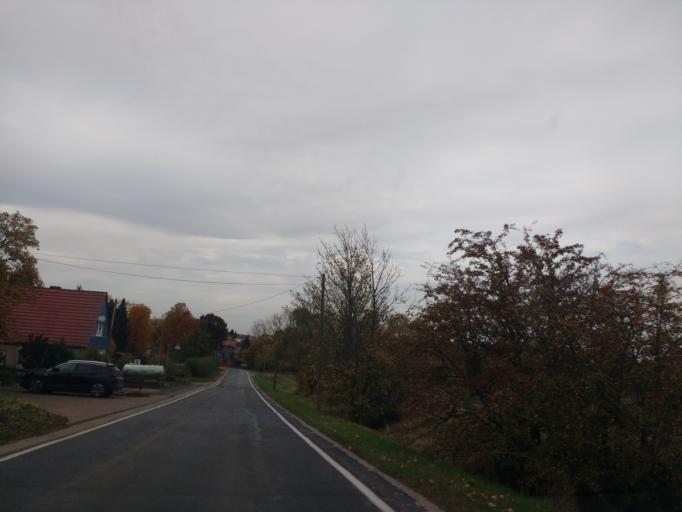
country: DE
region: Thuringia
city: Seebach
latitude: 51.1611
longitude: 10.5167
